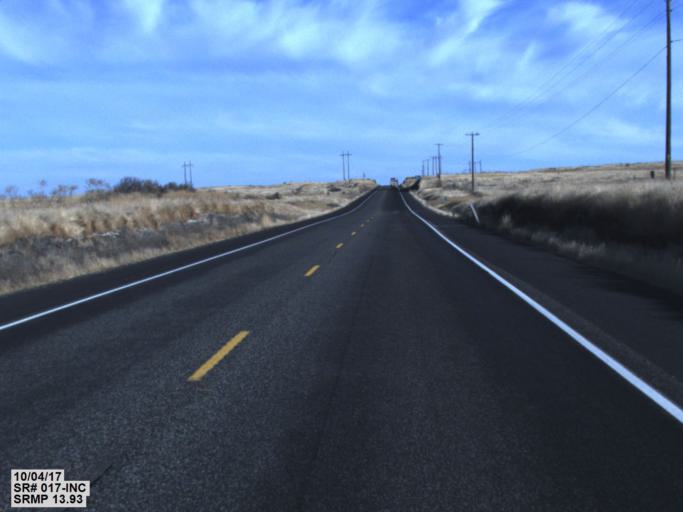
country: US
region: Washington
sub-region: Franklin County
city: Connell
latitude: 46.6540
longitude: -119.0064
